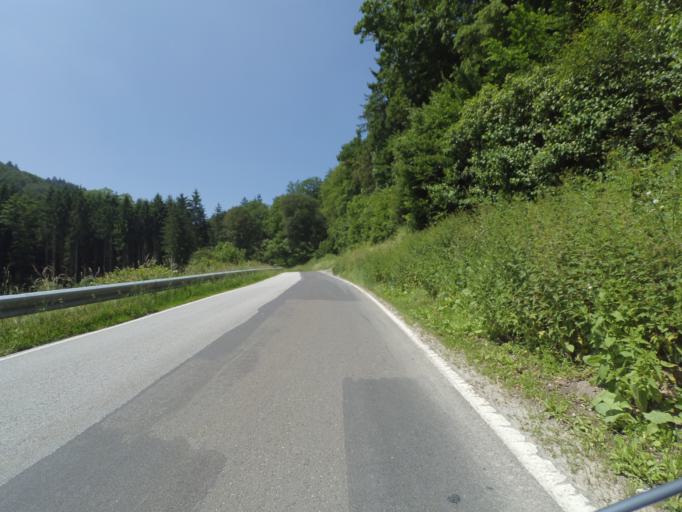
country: DE
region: Rheinland-Pfalz
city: Utzenhain
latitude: 50.1439
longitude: 7.6518
